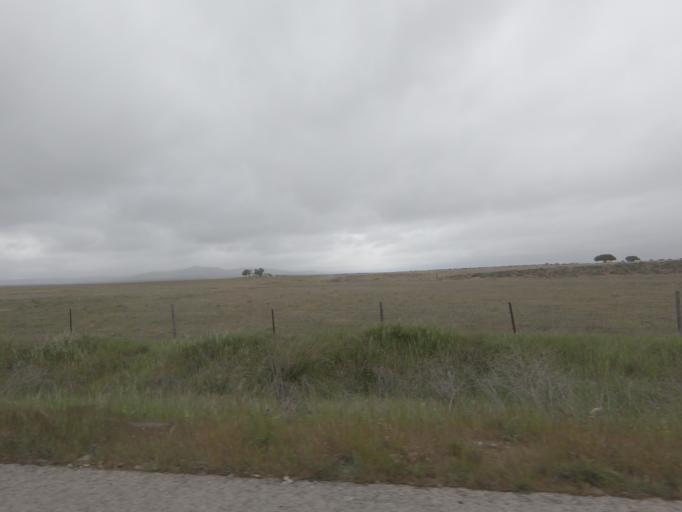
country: ES
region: Extremadura
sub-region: Provincia de Caceres
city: Malpartida de Caceres
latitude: 39.3533
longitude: -6.4680
